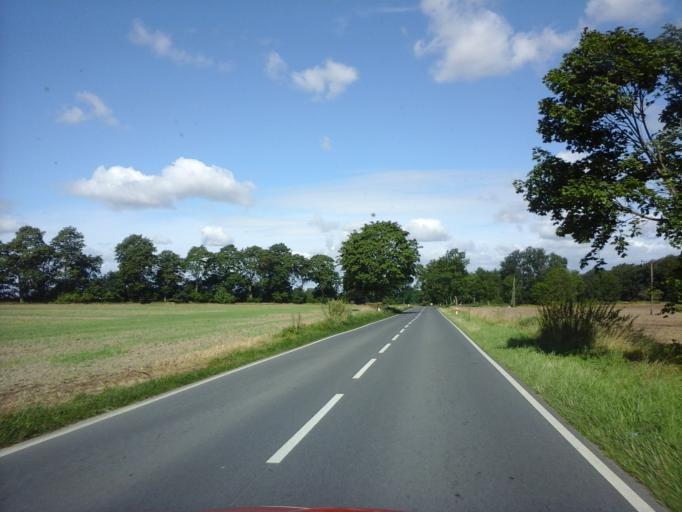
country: PL
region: West Pomeranian Voivodeship
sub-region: Powiat stargardzki
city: Dolice
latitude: 53.2041
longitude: 15.1496
